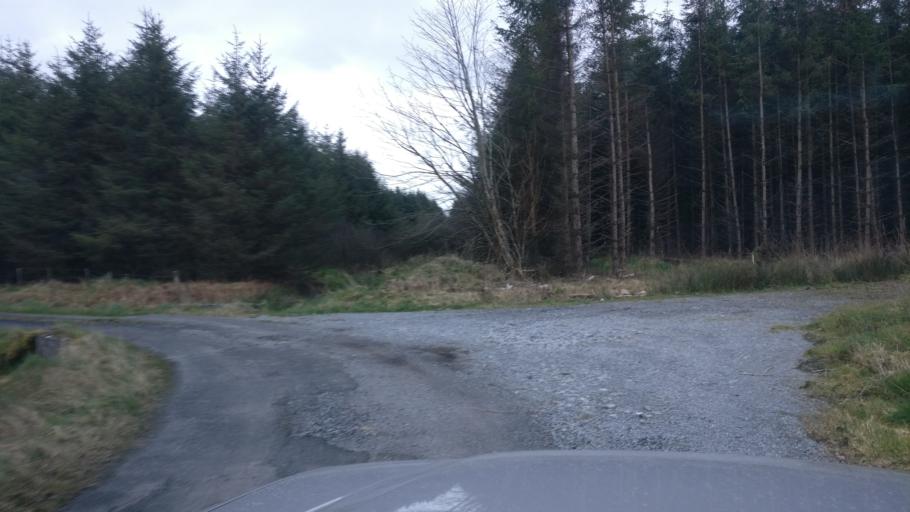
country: IE
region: Connaught
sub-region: County Galway
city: Loughrea
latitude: 53.2719
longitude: -8.4630
